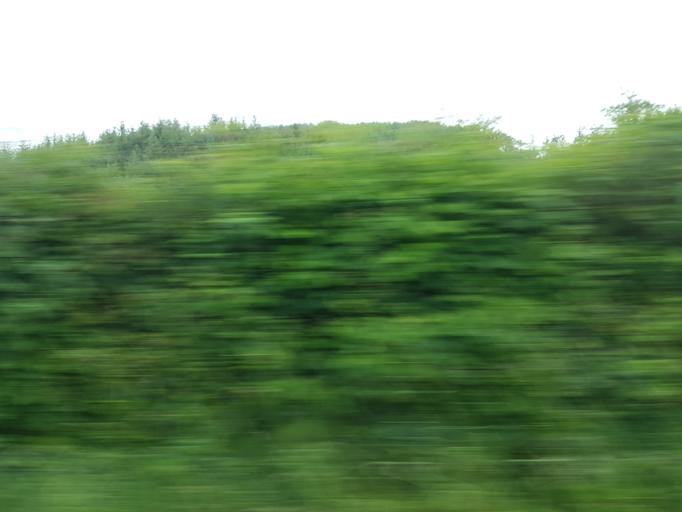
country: FR
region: Bourgogne
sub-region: Departement de la Nievre
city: Lormes
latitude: 47.1839
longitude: 3.8076
